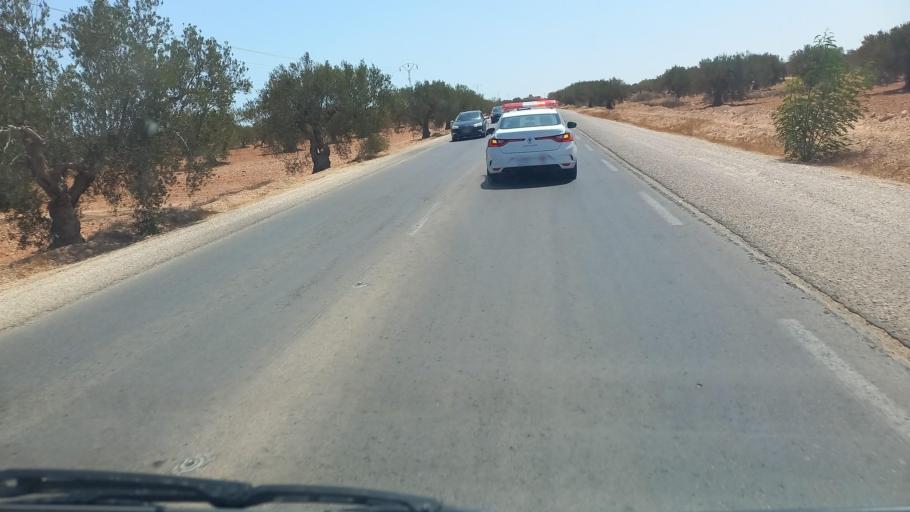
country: TN
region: Madanin
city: Zarzis
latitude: 33.5554
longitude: 11.0610
